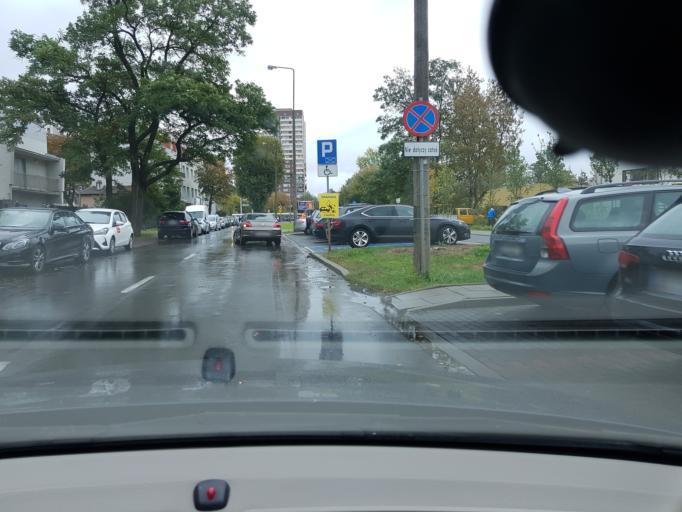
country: PL
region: Masovian Voivodeship
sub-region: Warszawa
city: Zoliborz
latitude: 52.2790
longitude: 20.9710
